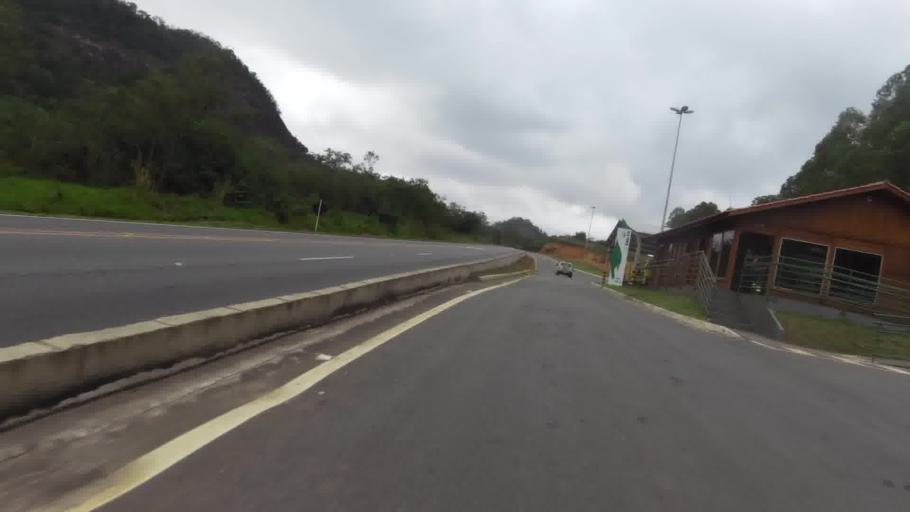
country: BR
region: Espirito Santo
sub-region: Alfredo Chaves
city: Alfredo Chaves
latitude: -20.7012
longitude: -40.7160
